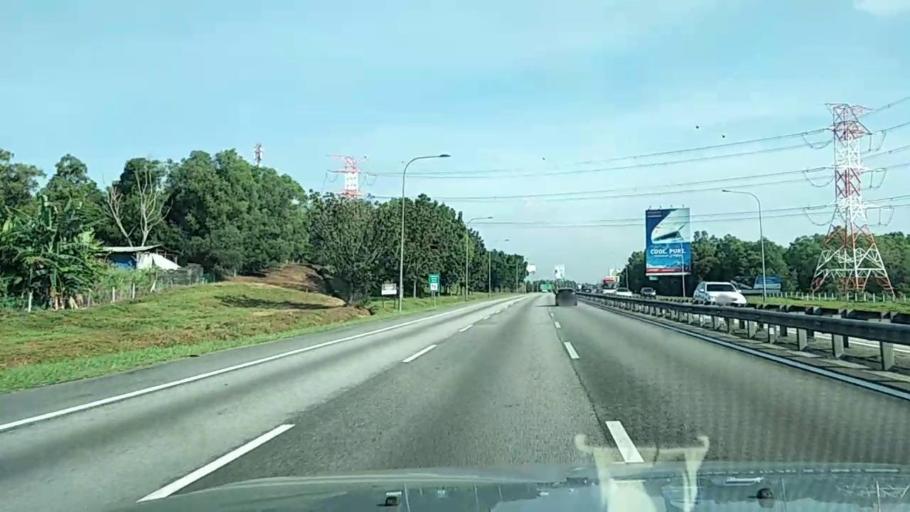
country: MY
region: Putrajaya
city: Putrajaya
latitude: 2.8613
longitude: 101.6434
